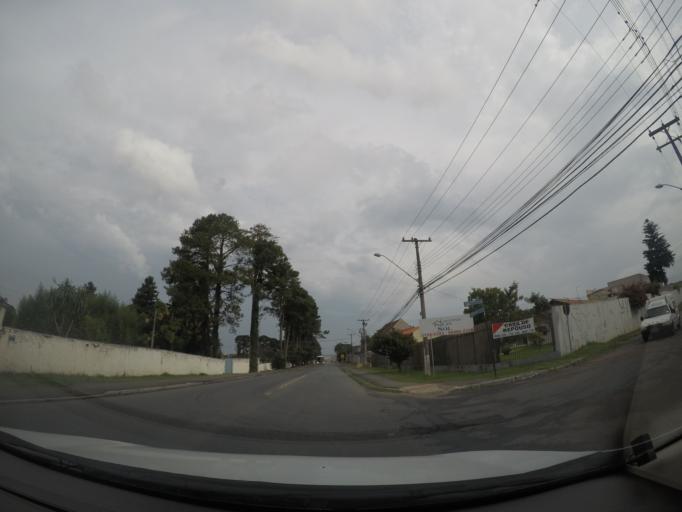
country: BR
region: Parana
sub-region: Sao Jose Dos Pinhais
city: Sao Jose dos Pinhais
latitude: -25.5162
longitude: -49.2612
